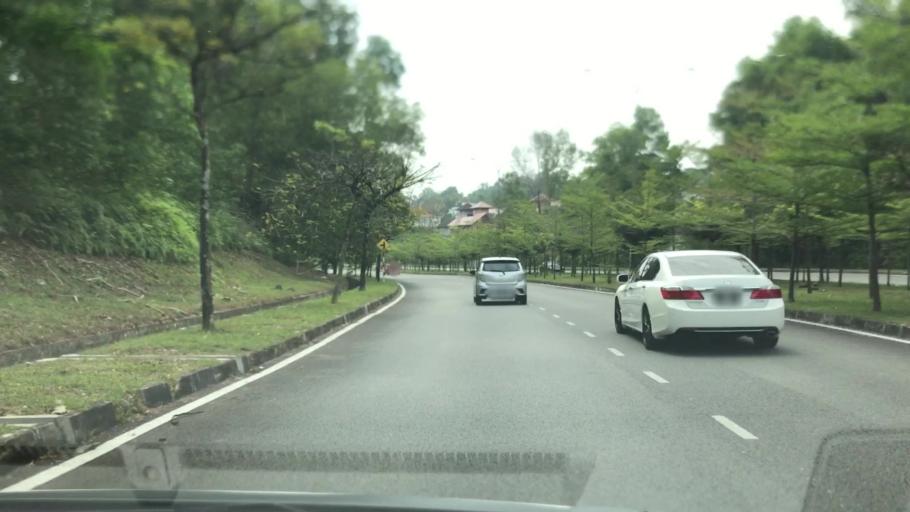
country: MY
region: Putrajaya
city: Putrajaya
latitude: 3.0051
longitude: 101.6678
